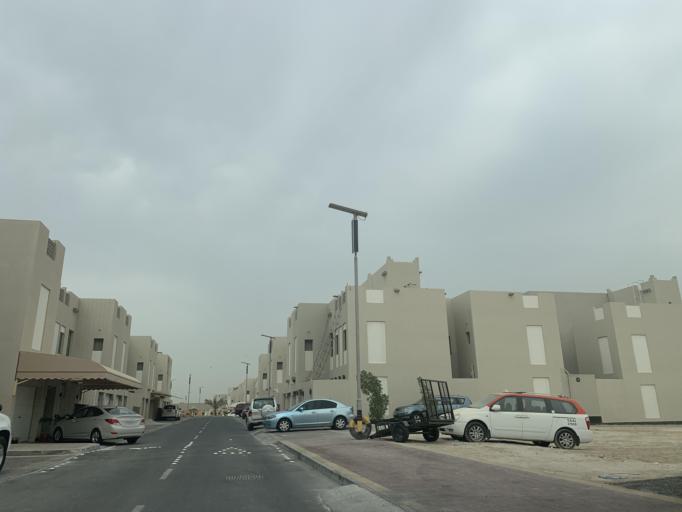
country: BH
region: Northern
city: Madinat `Isa
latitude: 26.1697
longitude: 50.5098
